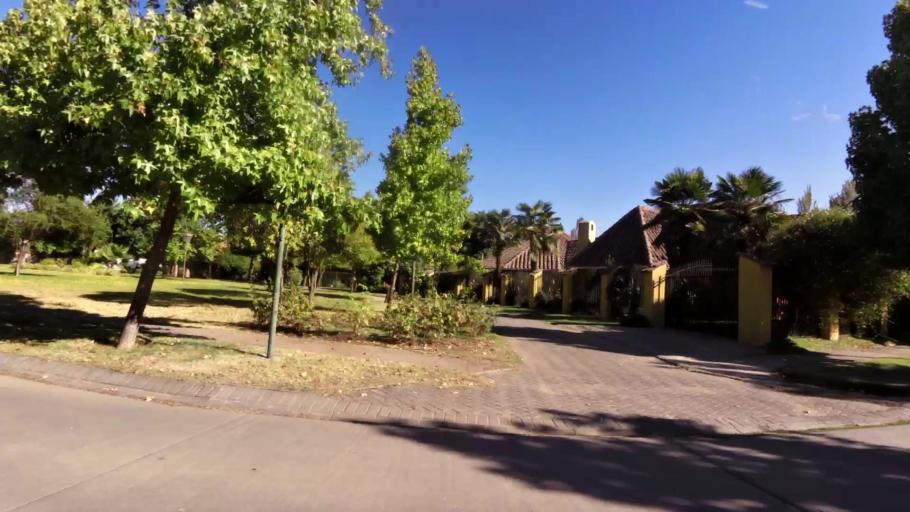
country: CL
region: O'Higgins
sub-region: Provincia de Cachapoal
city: Rancagua
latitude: -34.1901
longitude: -70.7154
